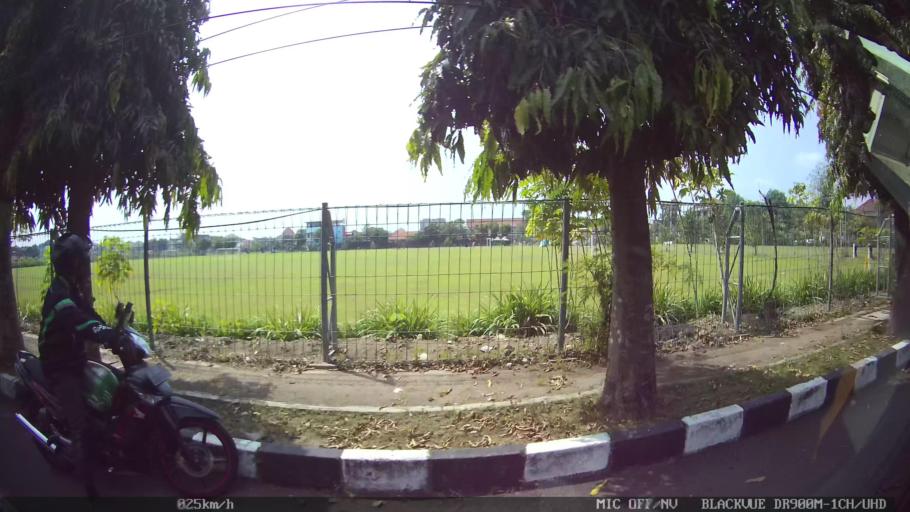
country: ID
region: Daerah Istimewa Yogyakarta
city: Yogyakarta
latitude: -7.7976
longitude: 110.3870
